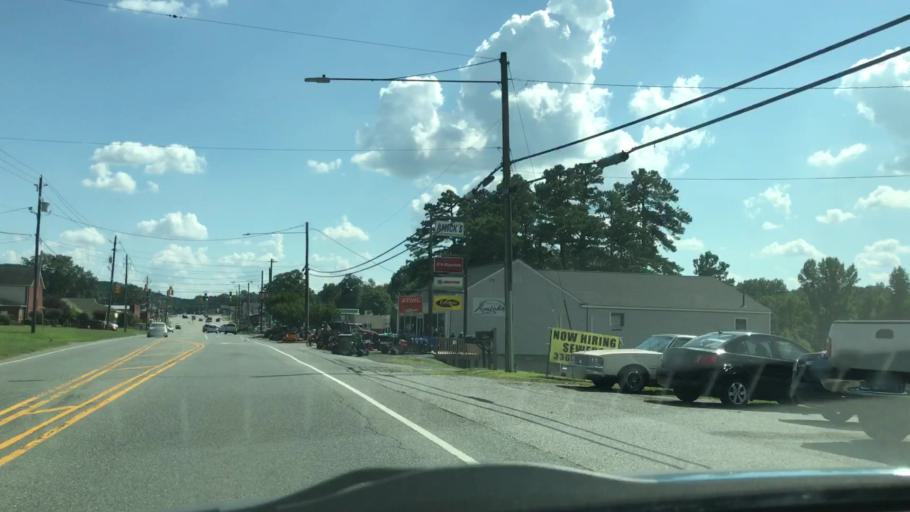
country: US
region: North Carolina
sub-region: Randolph County
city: Asheboro
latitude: 35.7412
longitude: -79.8083
